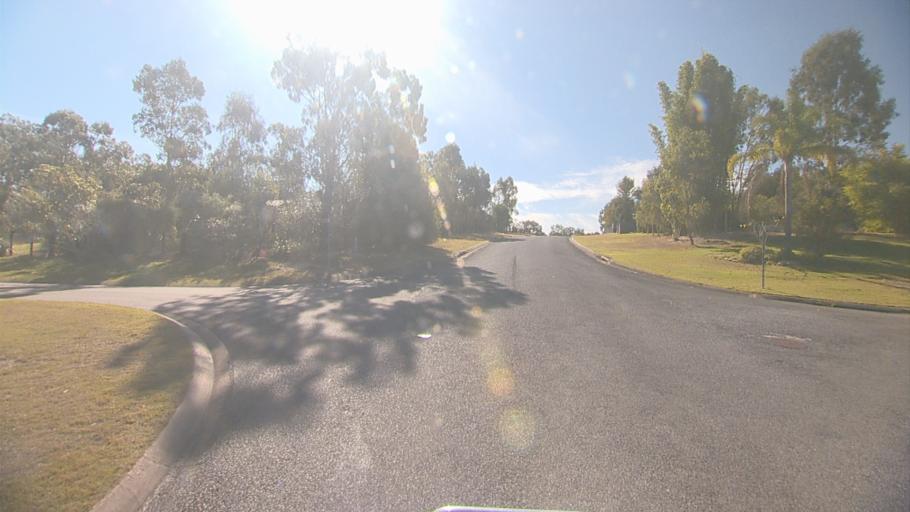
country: AU
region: Queensland
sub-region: Ipswich
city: Springfield Lakes
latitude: -27.7305
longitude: 152.9419
